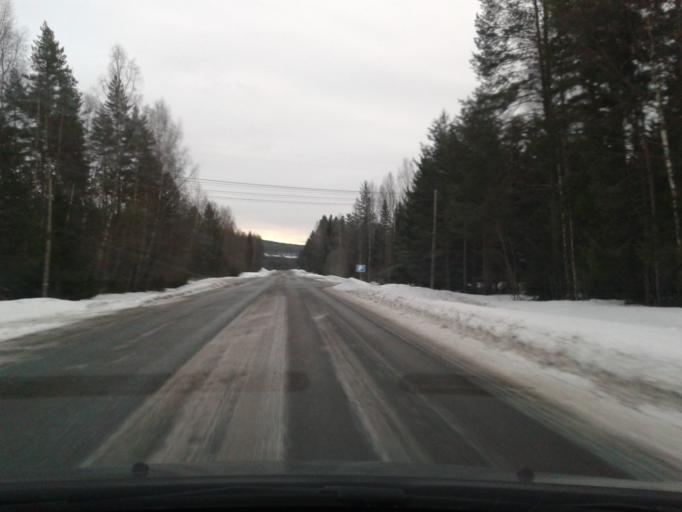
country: SE
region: Vaesternorrland
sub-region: Solleftea Kommun
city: Solleftea
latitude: 63.2974
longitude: 17.2136
